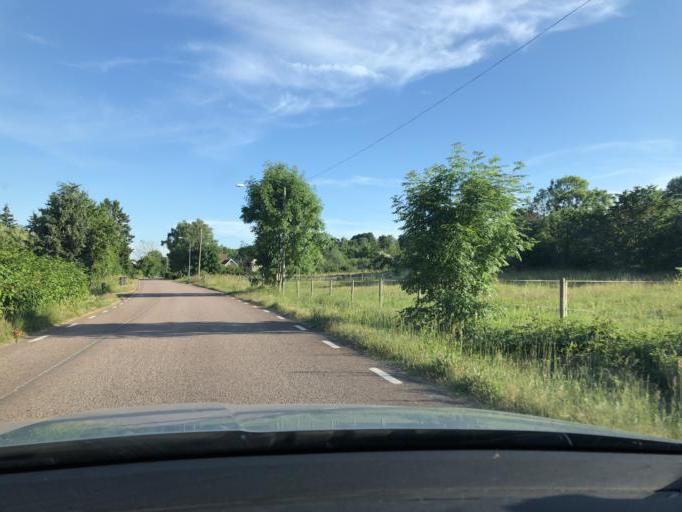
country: SE
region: Blekinge
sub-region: Solvesborgs Kommun
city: Soelvesborg
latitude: 56.1500
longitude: 14.6028
